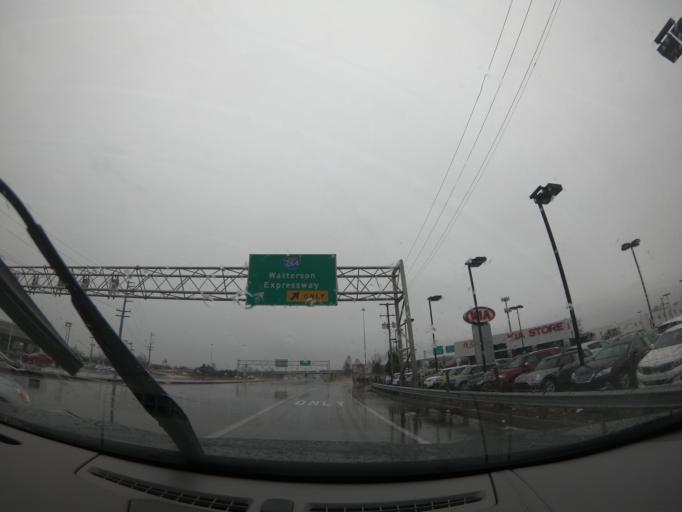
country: US
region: Kentucky
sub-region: Jefferson County
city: Lyndon
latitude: 38.2497
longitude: -85.6155
